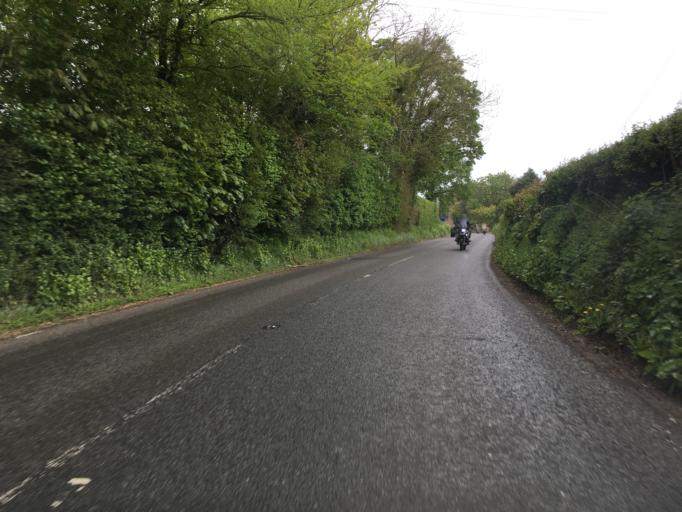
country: GB
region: England
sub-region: Bath and North East Somerset
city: Stanton Drew
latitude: 51.3432
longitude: -2.5779
